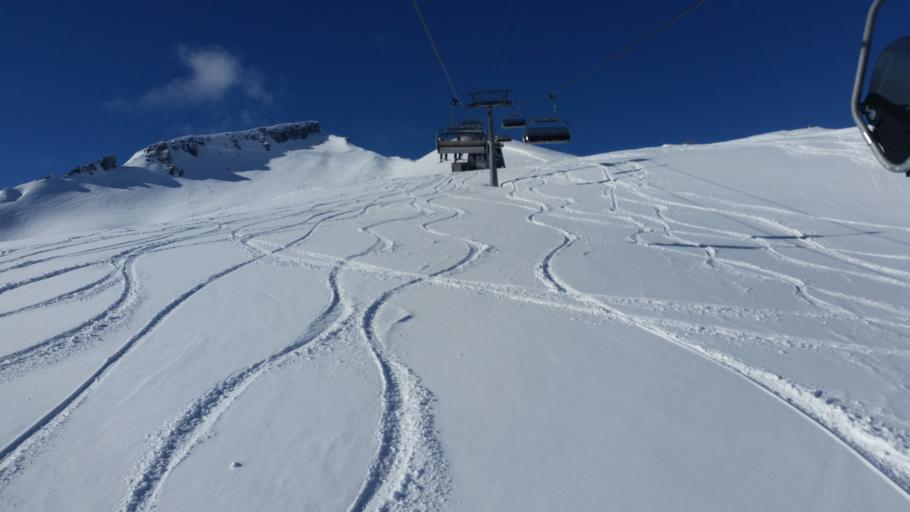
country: CH
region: Grisons
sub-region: Imboden District
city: Flims
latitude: 46.8672
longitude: 9.2218
